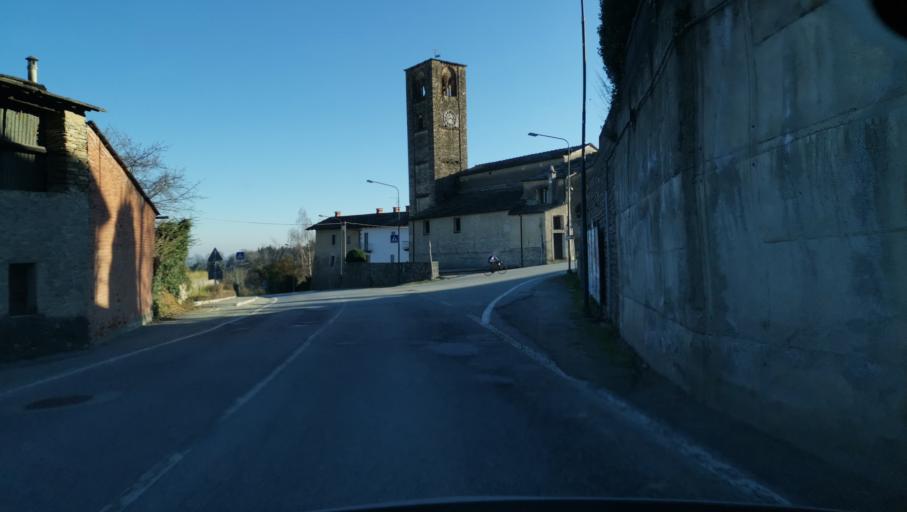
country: IT
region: Piedmont
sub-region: Provincia di Cuneo
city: Bagnolo Piemonte
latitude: 44.7534
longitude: 7.2901
